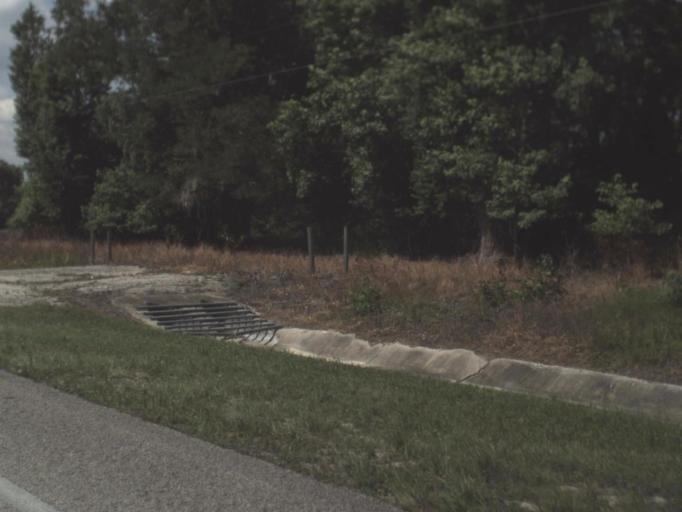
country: US
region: Florida
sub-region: Alachua County
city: Hawthorne
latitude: 29.6733
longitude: -82.1206
